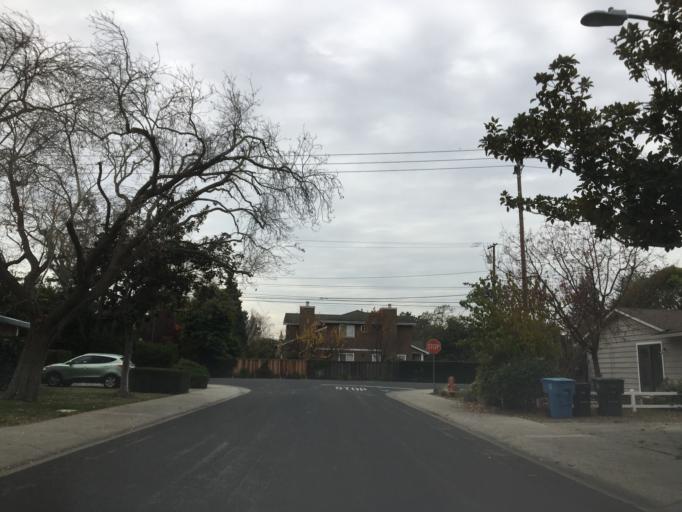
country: US
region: California
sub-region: Santa Clara County
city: Palo Alto
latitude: 37.4394
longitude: -122.1254
